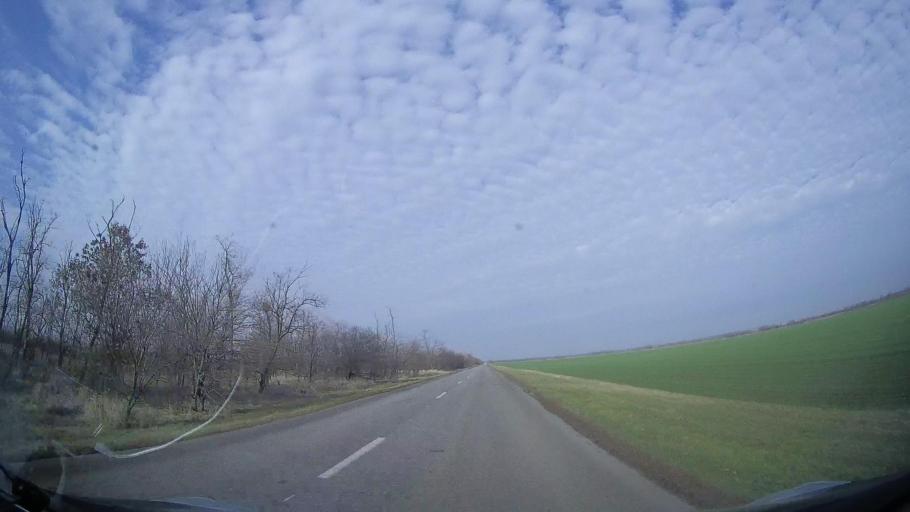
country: RU
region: Rostov
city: Gigant
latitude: 46.8641
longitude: 41.2780
